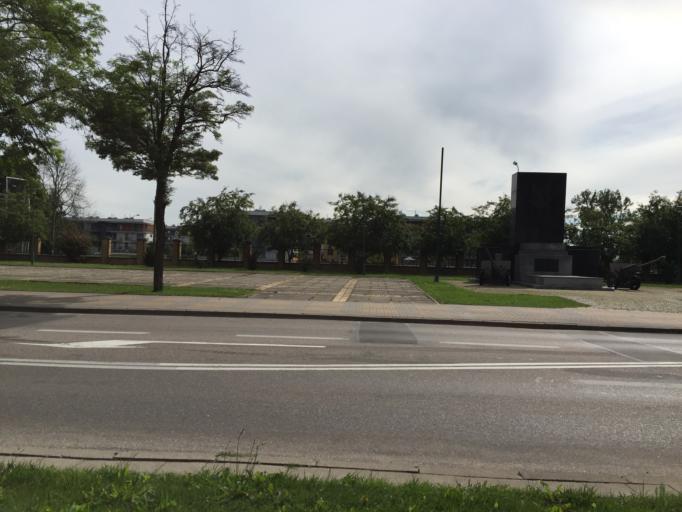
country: PL
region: Podlasie
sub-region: Suwalki
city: Suwalki
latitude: 54.0862
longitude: 22.9297
